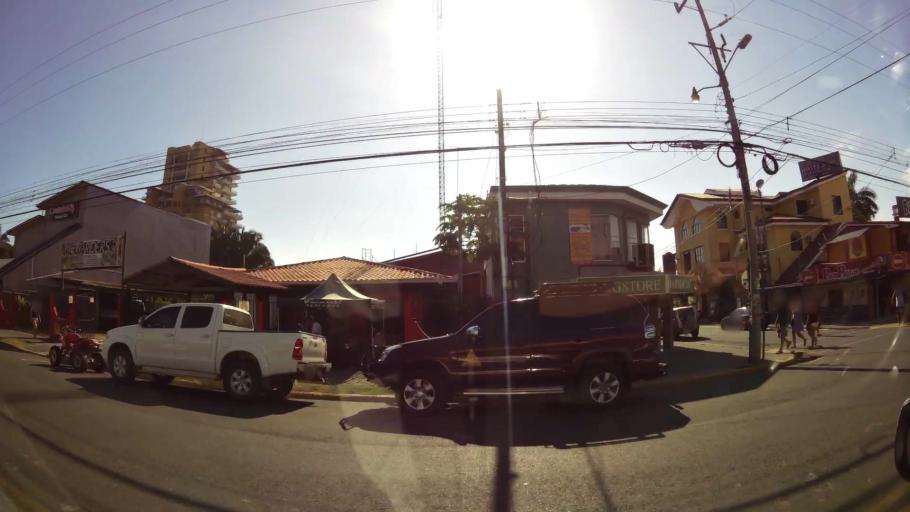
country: CR
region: Puntarenas
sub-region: Canton de Garabito
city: Jaco
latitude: 9.6127
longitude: -84.6268
